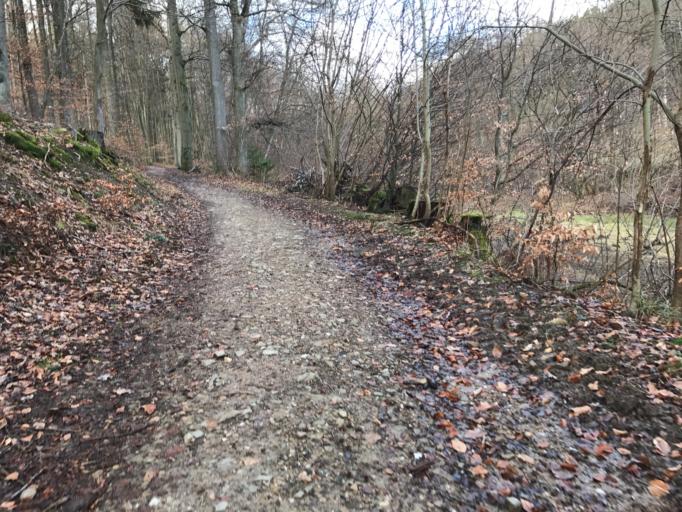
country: DE
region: Hesse
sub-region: Regierungsbezirk Darmstadt
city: Konigstein im Taunus
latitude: 50.2022
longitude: 8.4646
